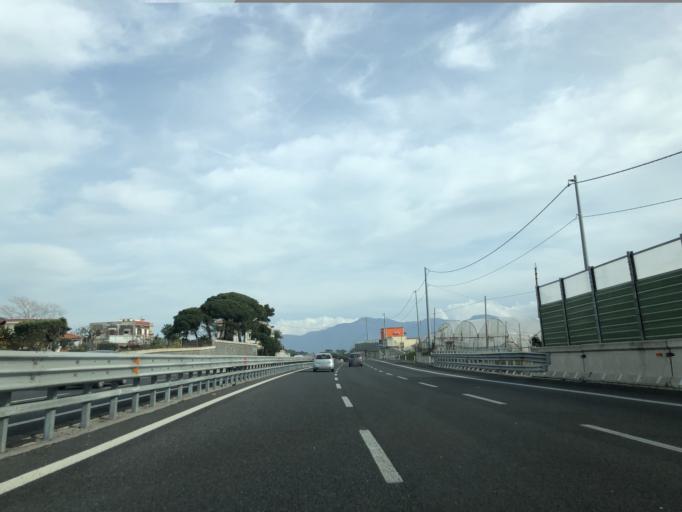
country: IT
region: Campania
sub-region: Provincia di Napoli
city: Torre del Greco
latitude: 40.7788
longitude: 14.3951
